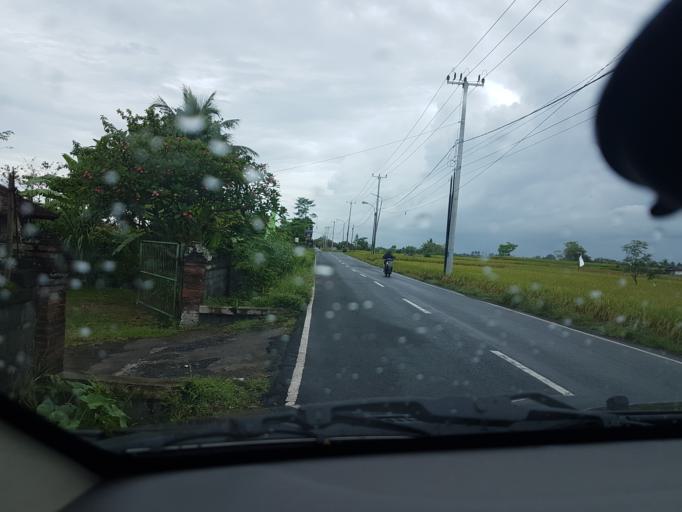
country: ID
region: Bali
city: Banjar Desa
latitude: -8.5797
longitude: 115.2337
